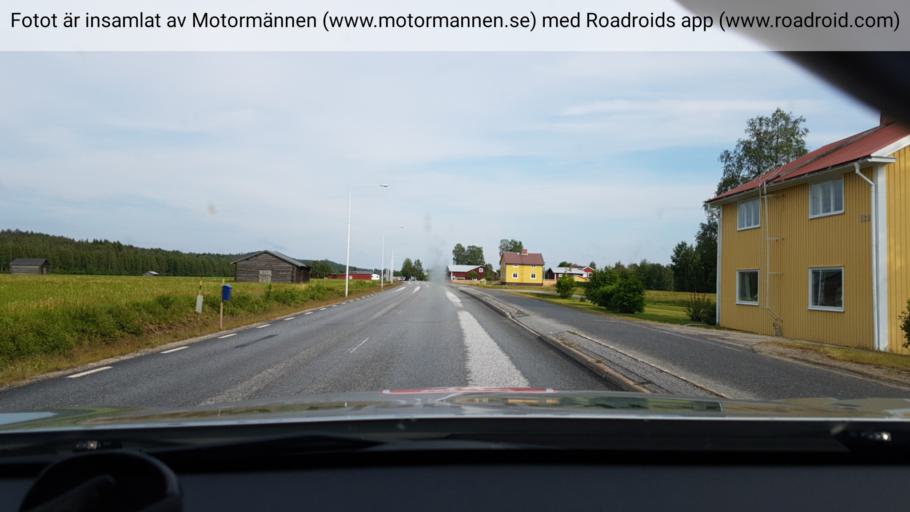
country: SE
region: Vaesterbotten
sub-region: Bjurholms Kommun
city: Bjurholm
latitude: 64.2596
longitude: 19.2863
